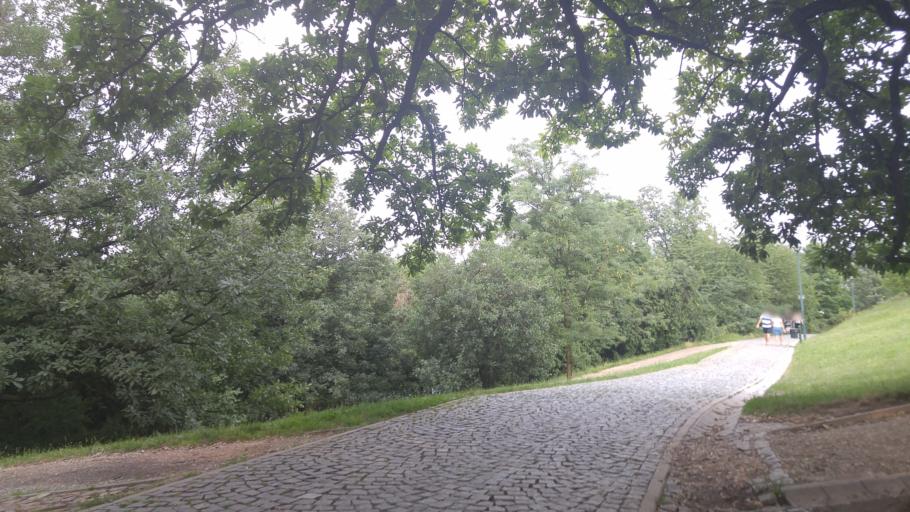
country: CZ
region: Praha
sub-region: Praha 1
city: Mala Strana
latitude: 50.0740
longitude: 14.3997
